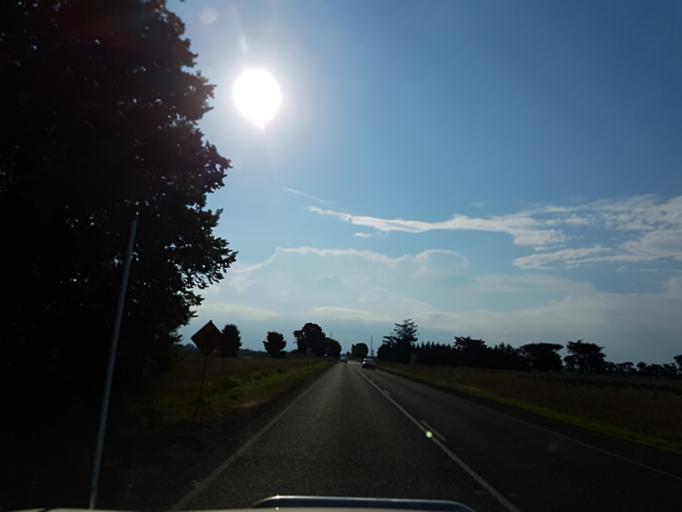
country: AU
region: Victoria
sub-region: Wellington
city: Sale
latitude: -38.0672
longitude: 147.0661
